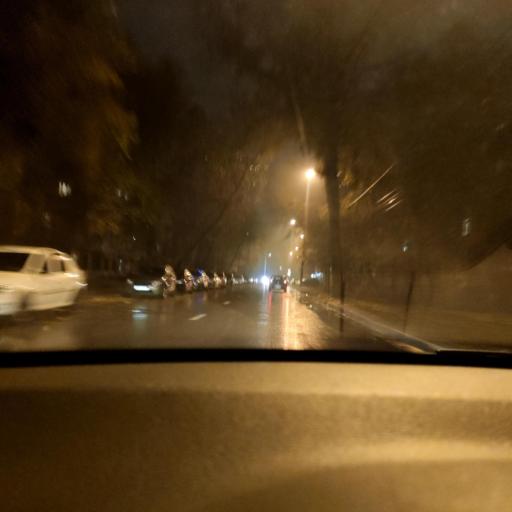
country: RU
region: Samara
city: Samara
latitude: 53.1946
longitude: 50.1739
